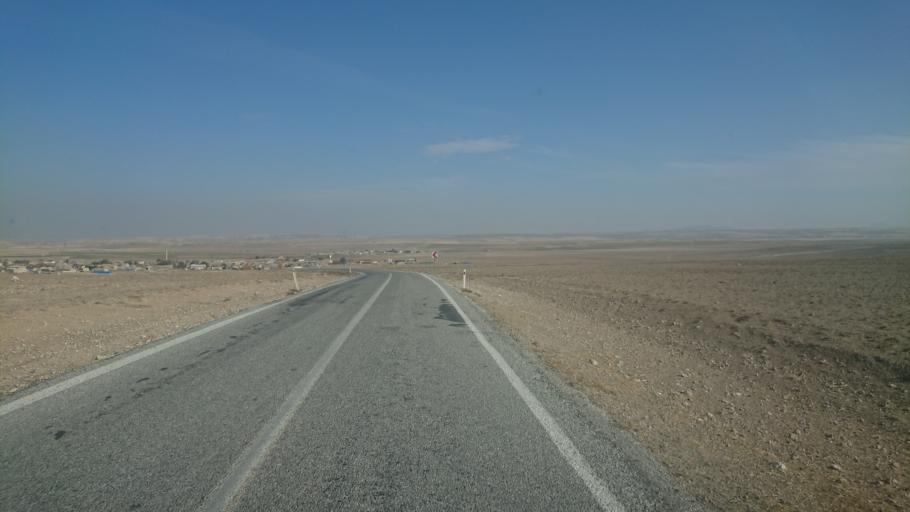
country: TR
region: Aksaray
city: Sultanhani
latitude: 38.0365
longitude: 33.5852
